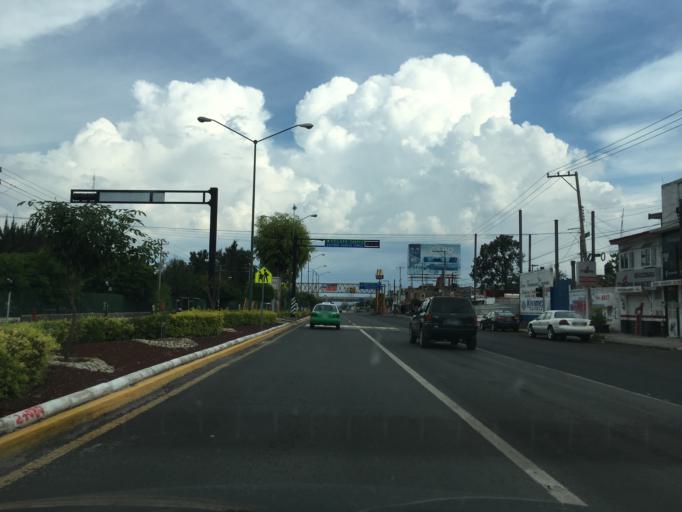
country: MX
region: Guanajuato
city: Celaya
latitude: 20.5396
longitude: -100.8202
